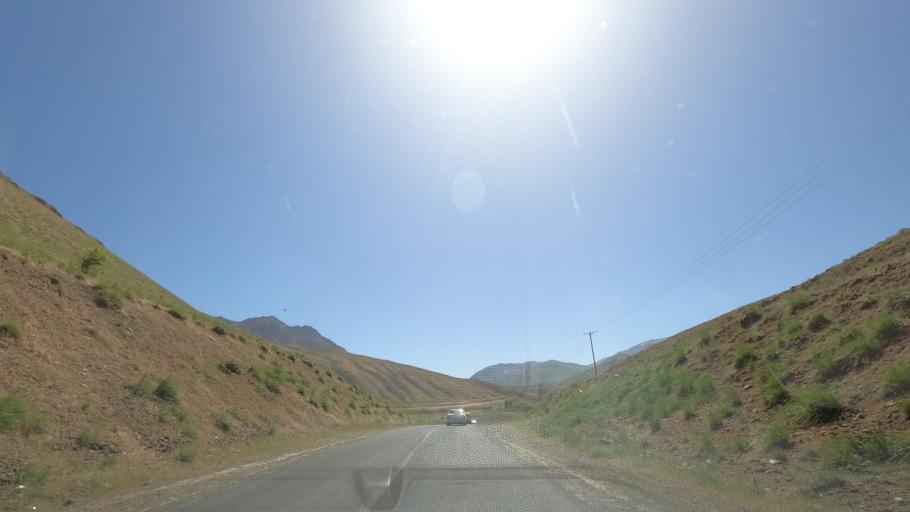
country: IR
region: Alborz
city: Karaj
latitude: 35.9259
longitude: 51.1013
